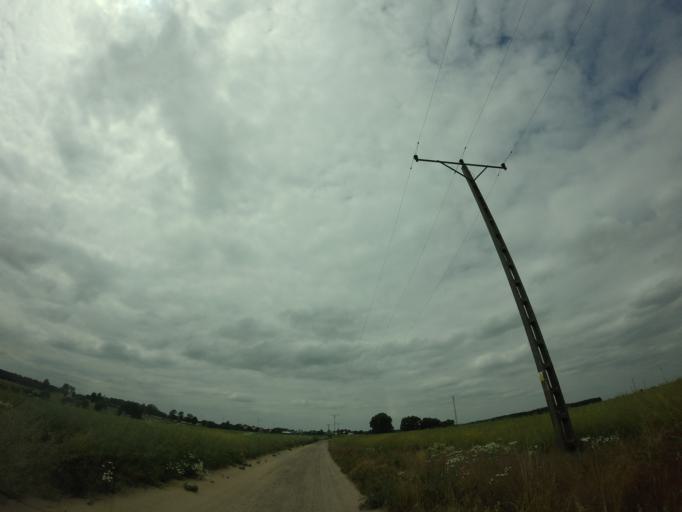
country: PL
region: West Pomeranian Voivodeship
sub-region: Powiat choszczenski
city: Krzecin
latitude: 53.0790
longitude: 15.5068
